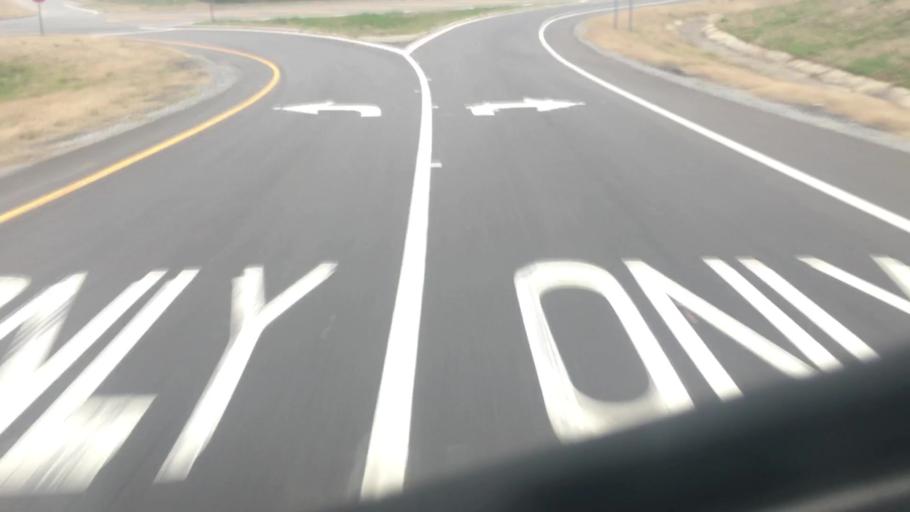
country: US
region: Alabama
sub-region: Walker County
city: Jasper
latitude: 33.7946
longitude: -87.2387
